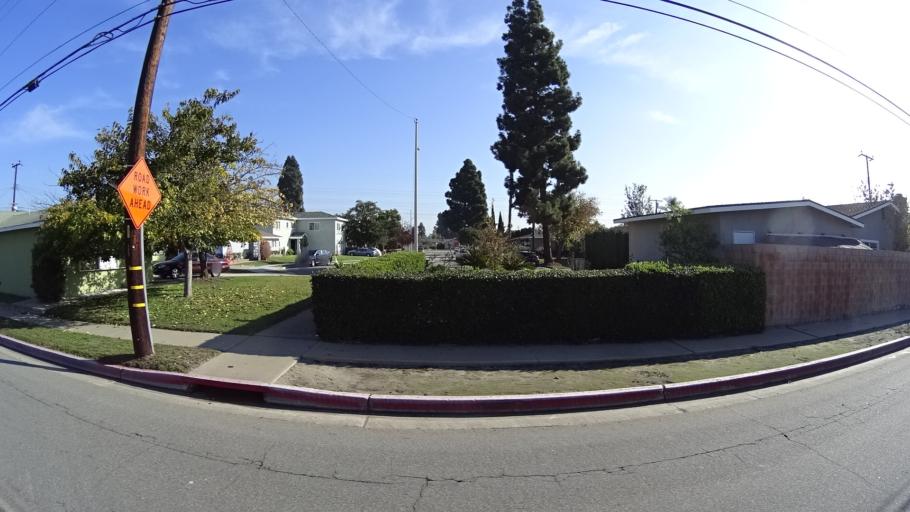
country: US
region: California
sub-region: Orange County
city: Midway City
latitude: 33.7216
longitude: -117.9806
